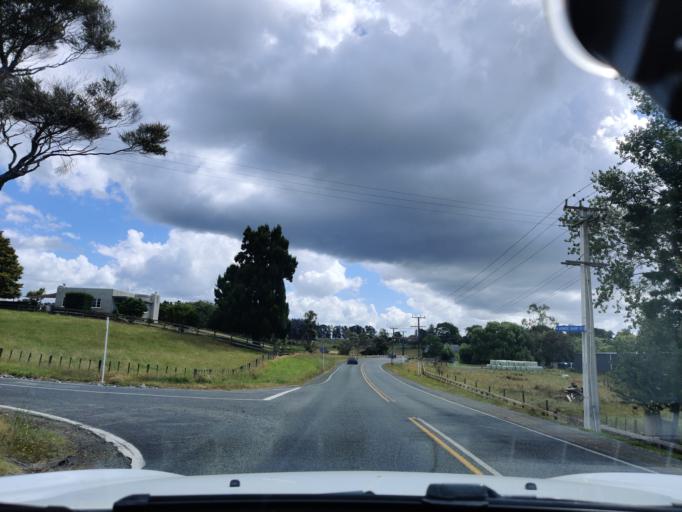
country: NZ
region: Auckland
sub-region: Auckland
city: Red Hill
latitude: -37.0386
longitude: 174.9928
